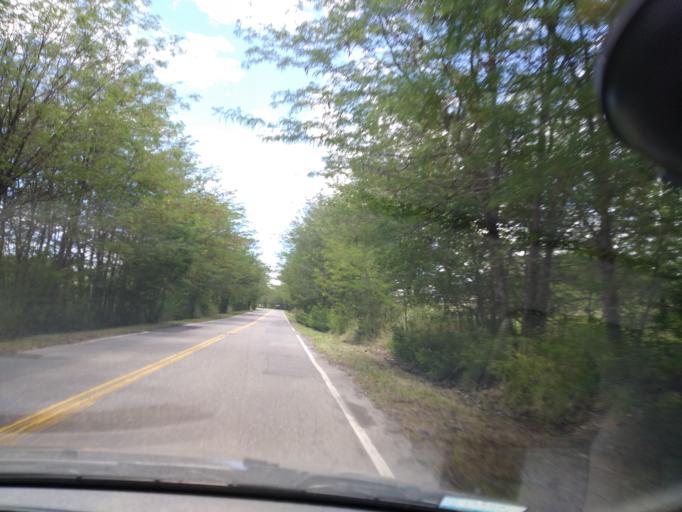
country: AR
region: Cordoba
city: Cuesta Blanca
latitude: -31.5960
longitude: -64.5650
